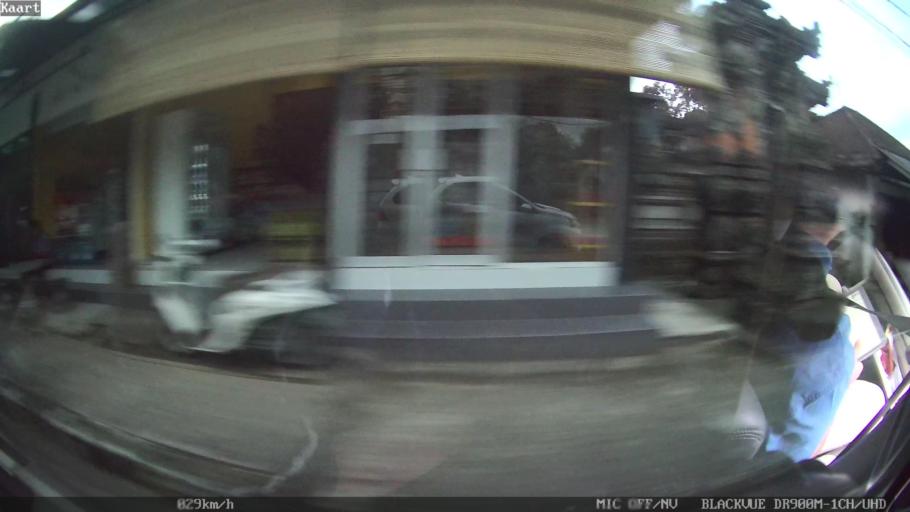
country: ID
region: Bali
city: Bunutan
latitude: -8.4841
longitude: 115.2463
